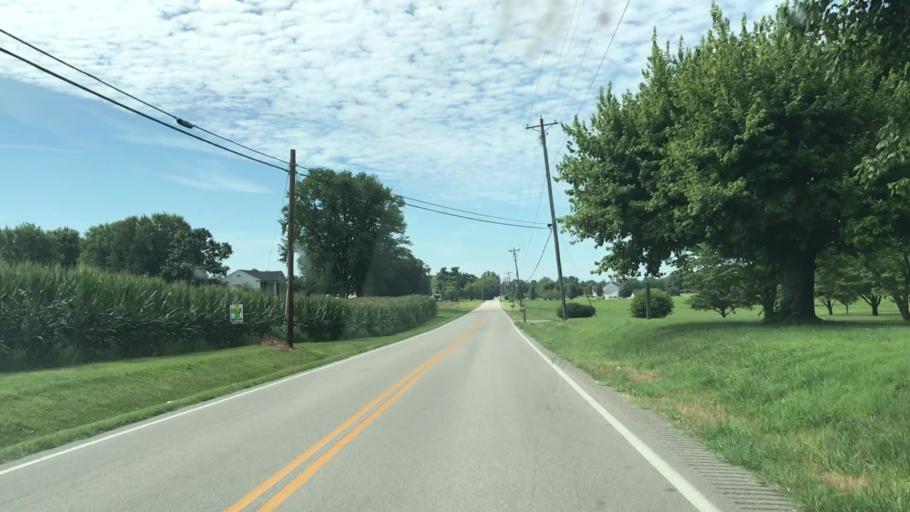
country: US
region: Kentucky
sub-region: Edmonson County
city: Brownsville
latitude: 37.0680
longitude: -86.2115
